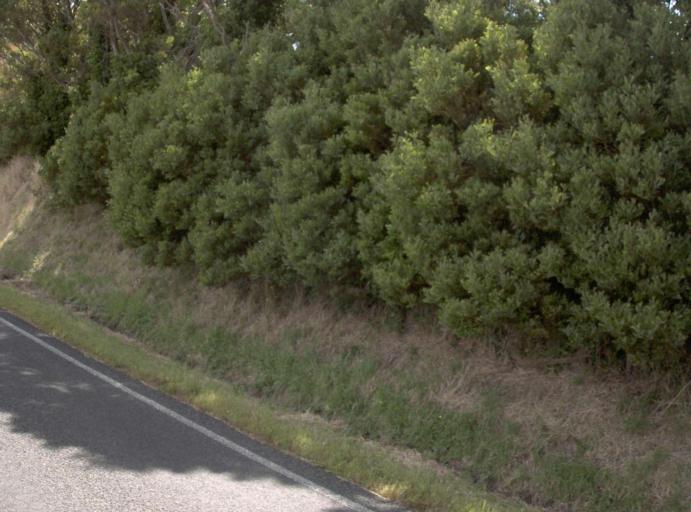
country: AU
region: Victoria
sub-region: Baw Baw
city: Warragul
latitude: -38.4025
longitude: 145.8347
